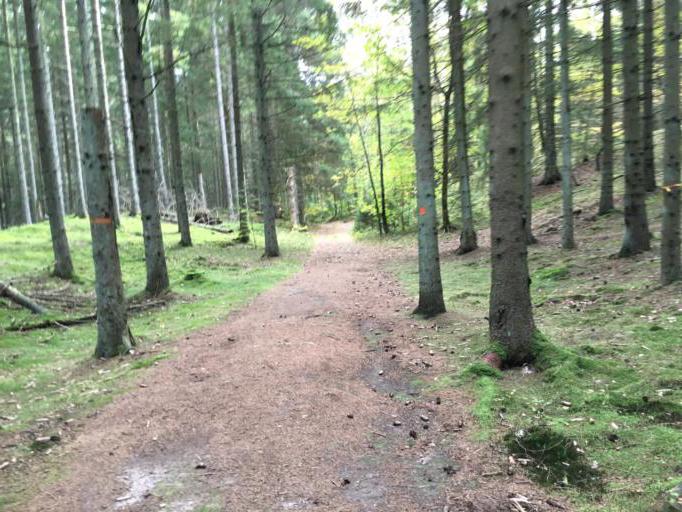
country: SE
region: Skane
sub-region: Hassleholms Kommun
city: Bjarnum
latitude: 56.2134
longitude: 13.6410
